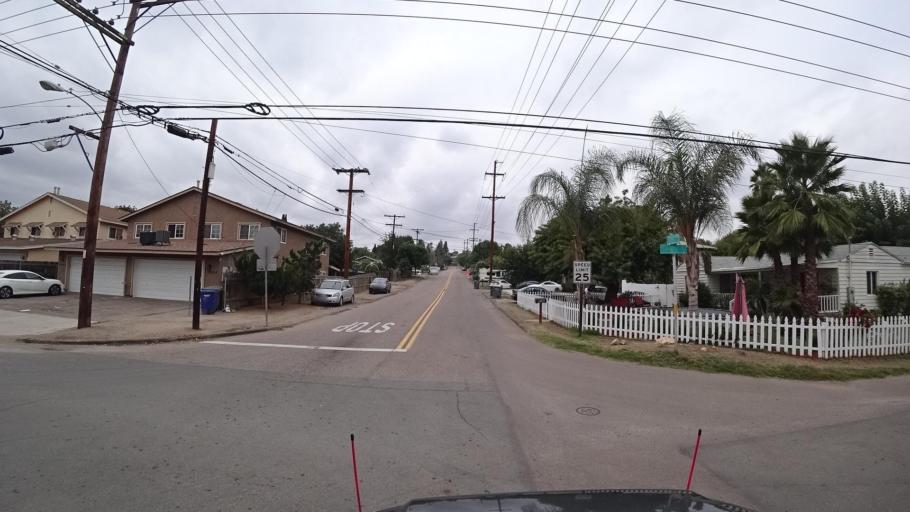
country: US
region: California
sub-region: San Diego County
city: Spring Valley
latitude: 32.7388
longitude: -117.0102
